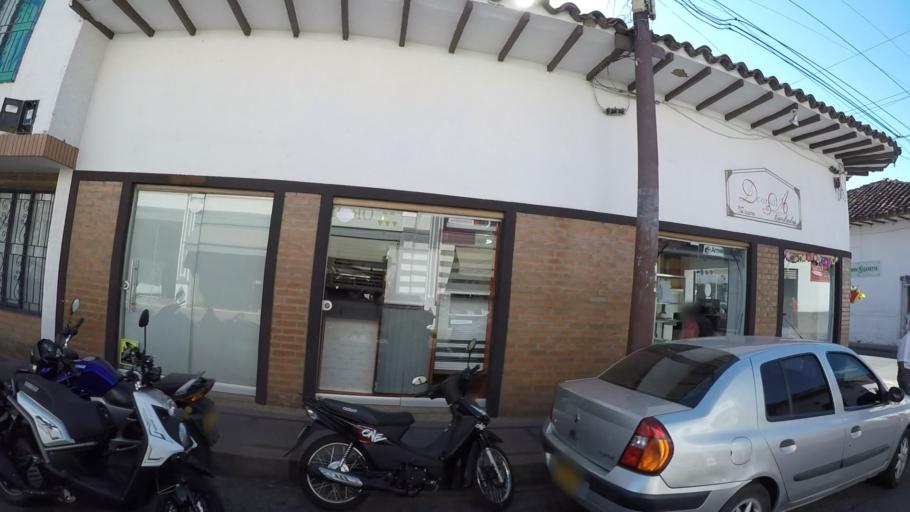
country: CO
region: Valle del Cauca
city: Cartago
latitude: 4.7494
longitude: -75.9083
